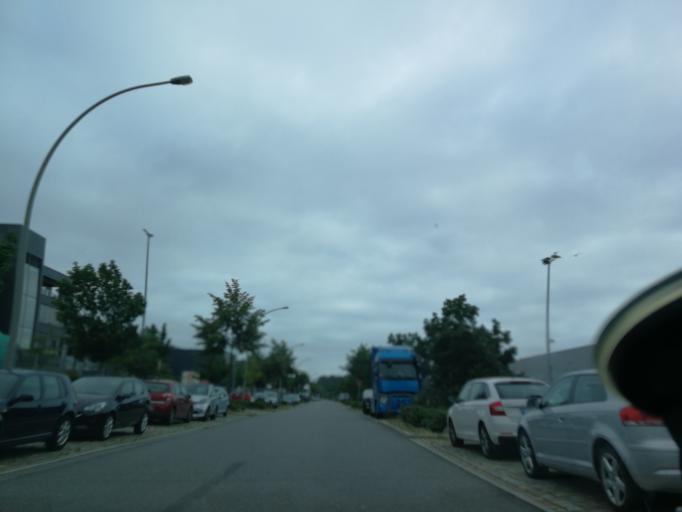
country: DE
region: Hamburg
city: Altona
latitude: 53.5045
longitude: 9.9259
